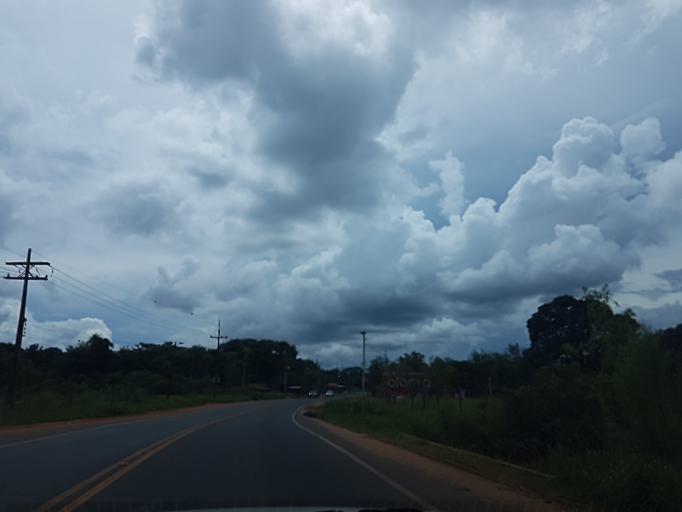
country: PY
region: Central
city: Limpio
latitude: -25.2369
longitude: -57.4394
